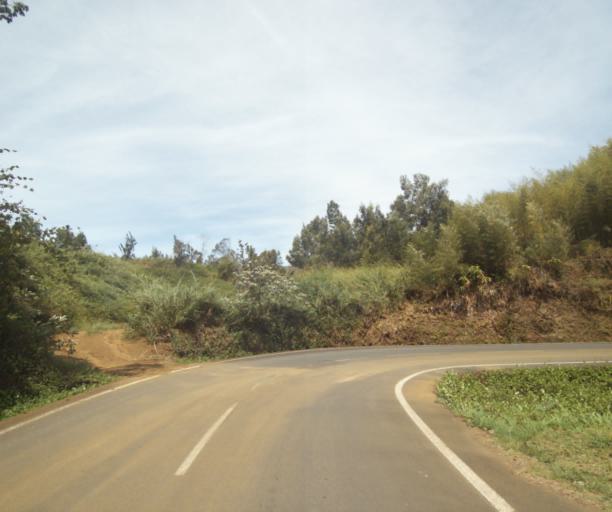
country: RE
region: Reunion
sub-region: Reunion
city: Trois-Bassins
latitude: -21.0682
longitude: 55.3092
